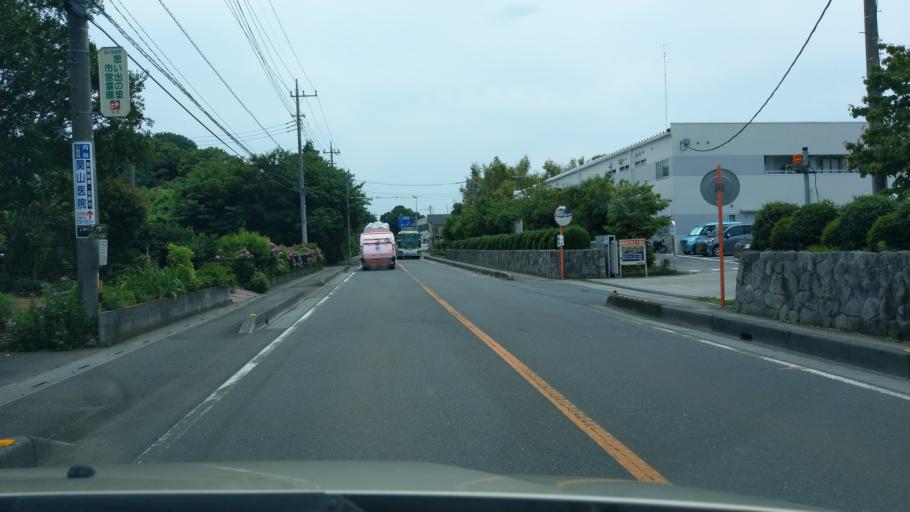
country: JP
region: Saitama
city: Saitama
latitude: 35.9108
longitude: 139.6951
